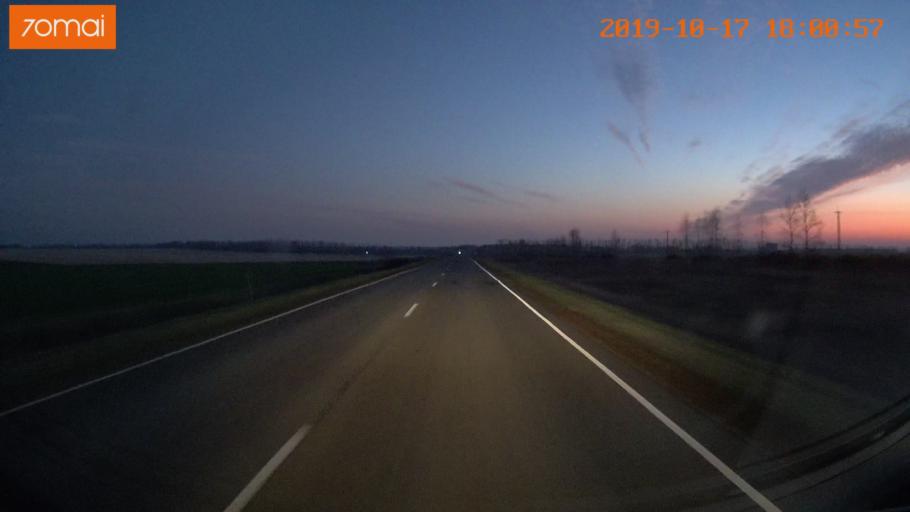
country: RU
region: Tula
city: Kurkino
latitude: 53.5144
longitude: 38.6126
